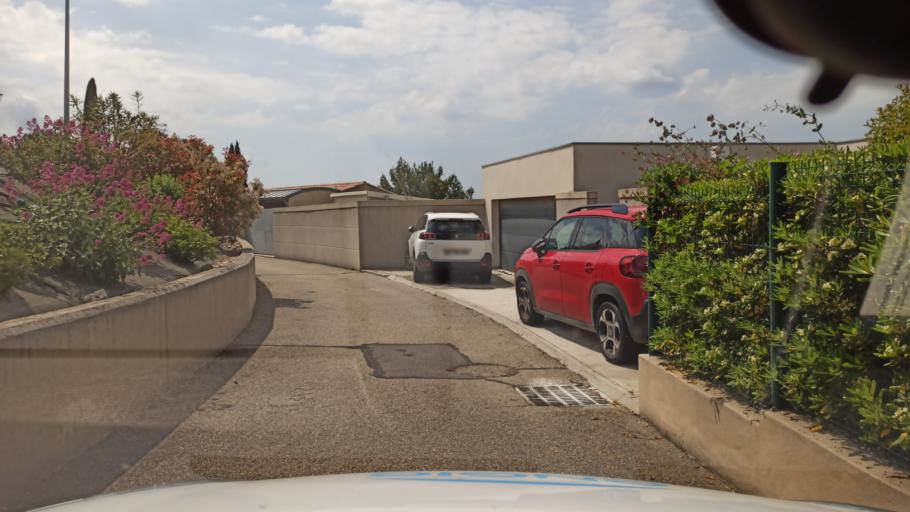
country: FR
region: Languedoc-Roussillon
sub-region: Departement du Gard
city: Les Angles
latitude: 43.9700
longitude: 4.7759
